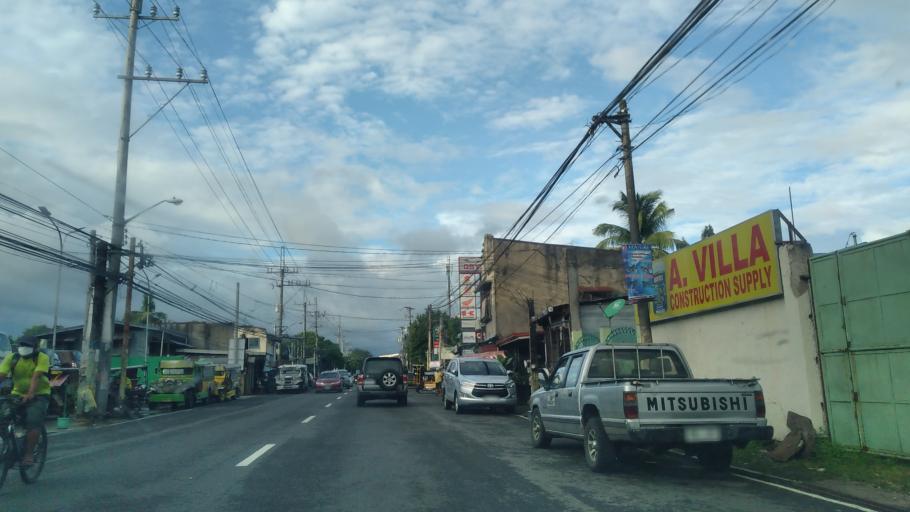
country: PH
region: Calabarzon
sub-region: Province of Quezon
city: Lucena
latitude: 13.9472
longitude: 121.6142
